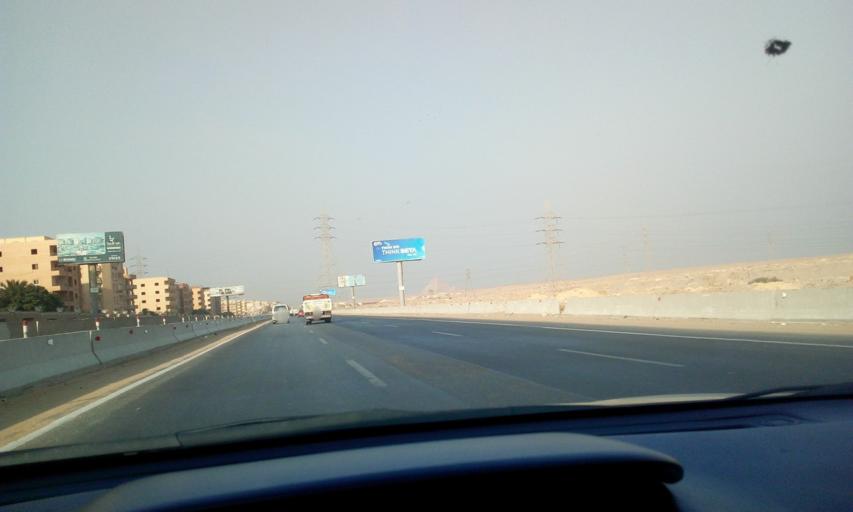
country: EG
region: Al Jizah
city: Al Jizah
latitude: 29.9482
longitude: 31.1004
